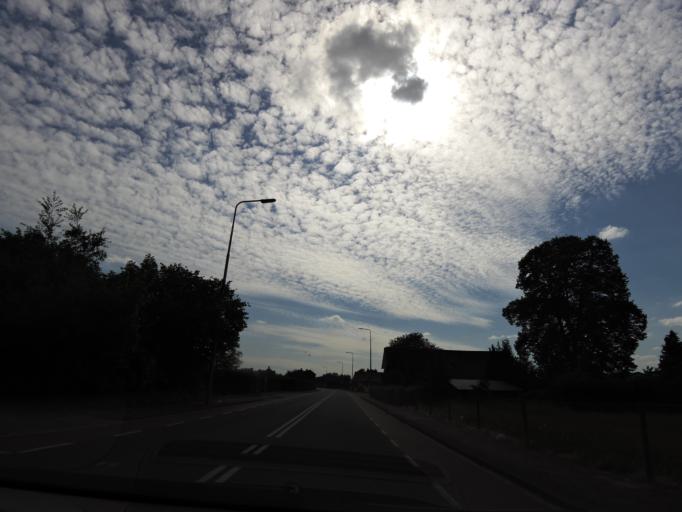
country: NL
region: Limburg
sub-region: Gemeente Echt-Susteren
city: Koningsbosch
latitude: 51.0627
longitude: 5.9681
